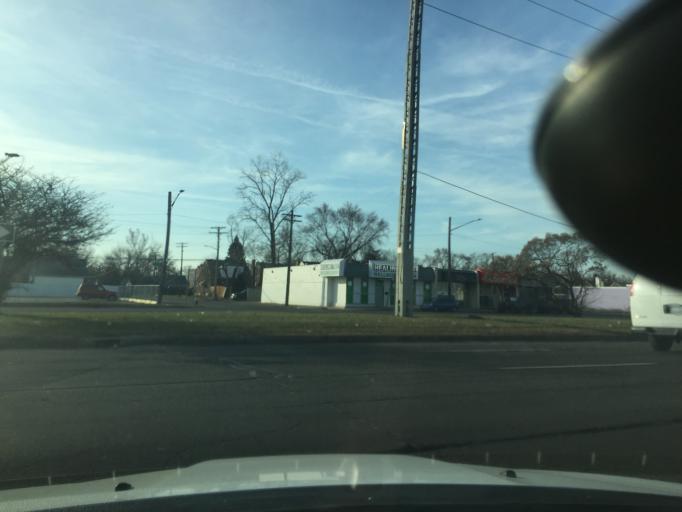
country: US
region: Michigan
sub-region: Macomb County
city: Eastpointe
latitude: 42.4503
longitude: -82.9634
